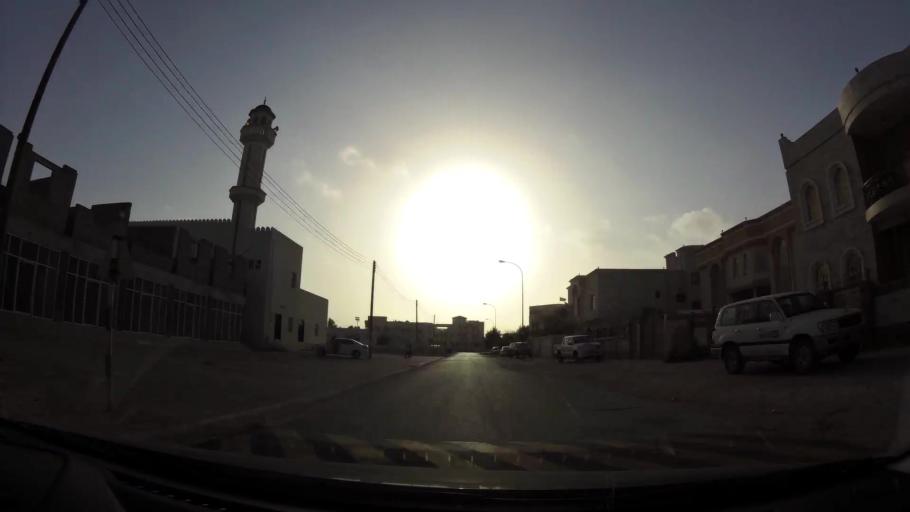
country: OM
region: Zufar
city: Salalah
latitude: 16.9948
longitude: 54.0280
